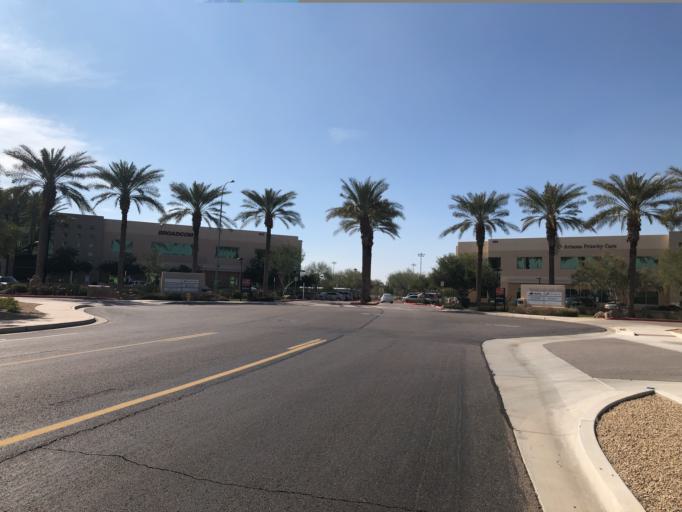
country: US
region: Arizona
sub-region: Maricopa County
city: San Carlos
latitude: 33.3113
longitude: -111.9160
